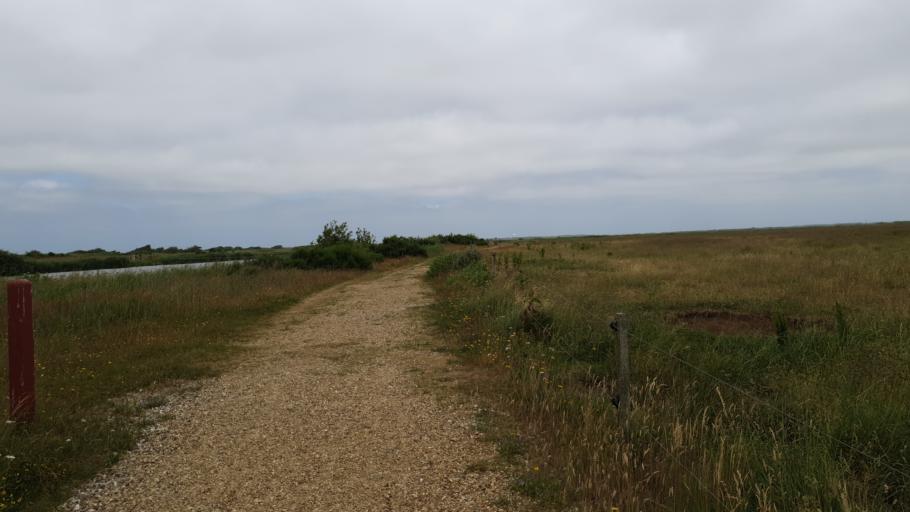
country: DK
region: Central Jutland
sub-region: Ringkobing-Skjern Kommune
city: Skjern
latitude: 55.9168
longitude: 8.4075
